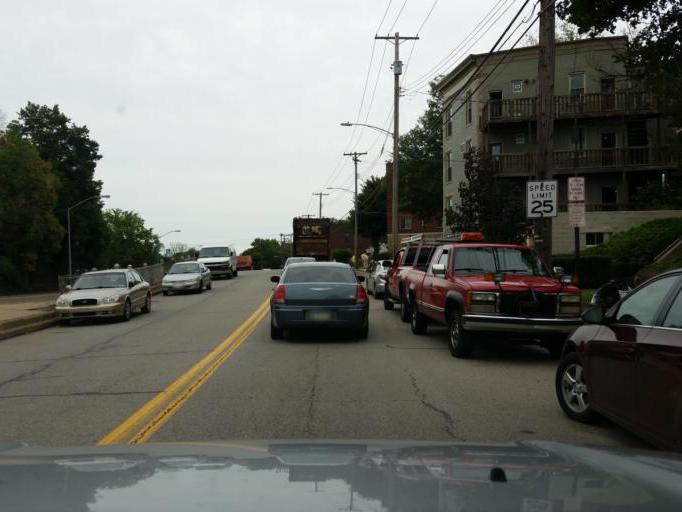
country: US
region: Pennsylvania
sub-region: Allegheny County
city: Edgewood
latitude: 40.4309
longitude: -79.8845
